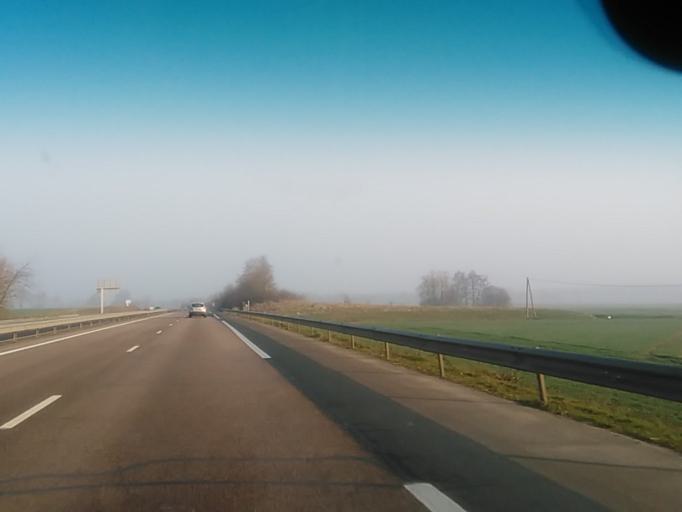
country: FR
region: Lower Normandy
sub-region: Departement du Calvados
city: Potigny
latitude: 48.9570
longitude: -0.2260
